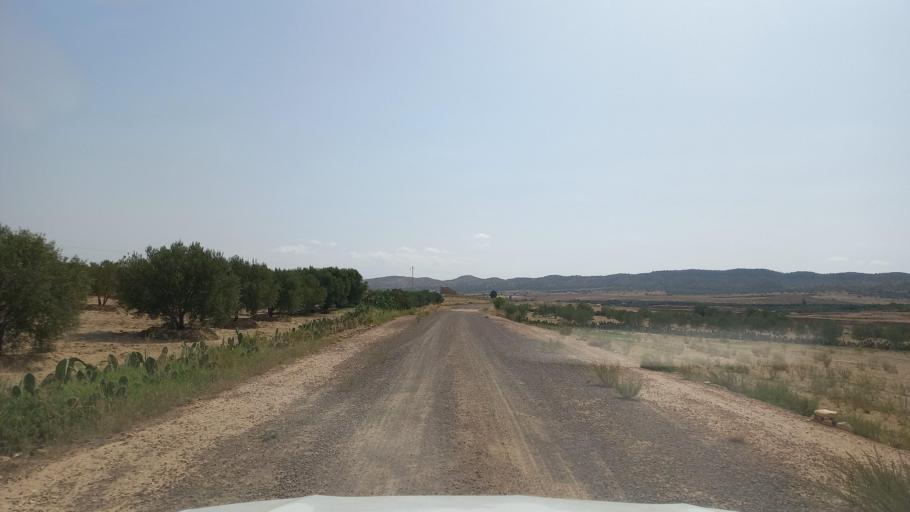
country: TN
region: Al Qasrayn
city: Sbiba
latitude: 35.3930
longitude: 8.9558
